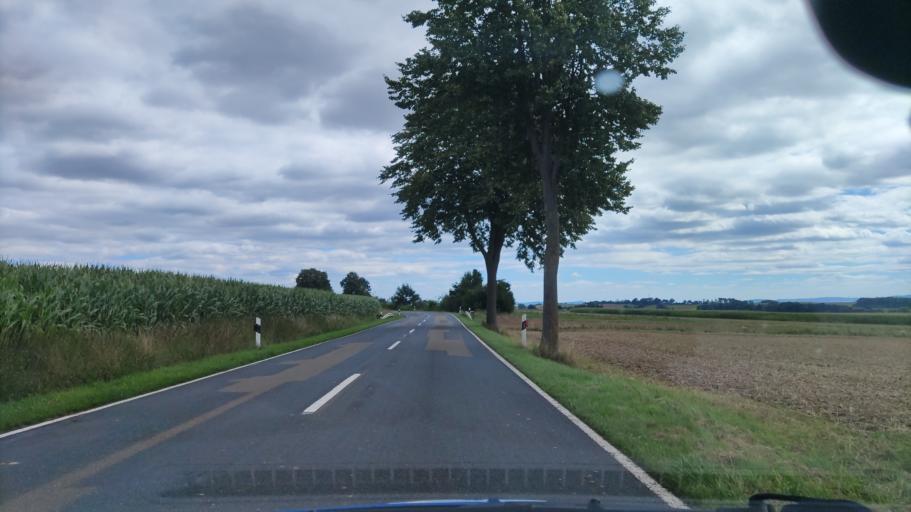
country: DE
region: Lower Saxony
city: Eimen
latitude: 51.8378
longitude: 9.7428
